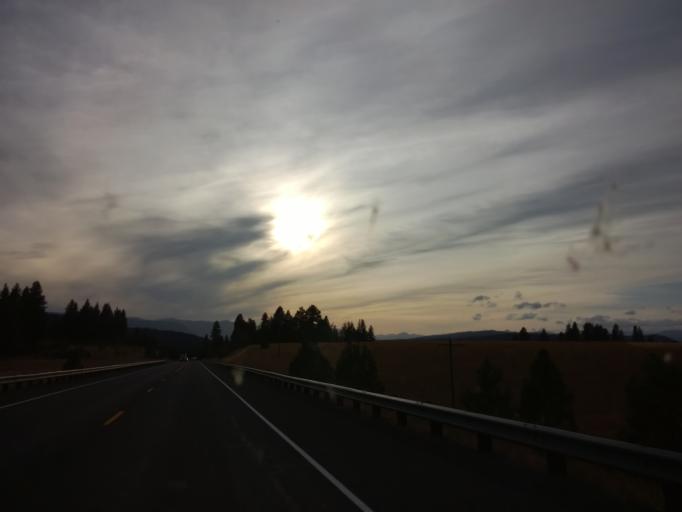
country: US
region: Washington
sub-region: Kittitas County
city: Cle Elum
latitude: 47.1985
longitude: -120.7443
